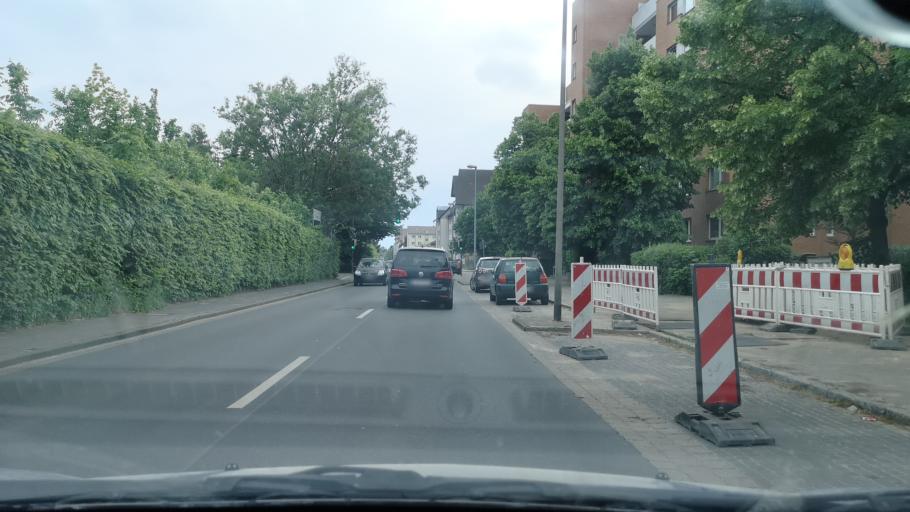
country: DE
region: Lower Saxony
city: Hannover
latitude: 52.4054
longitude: 9.6946
